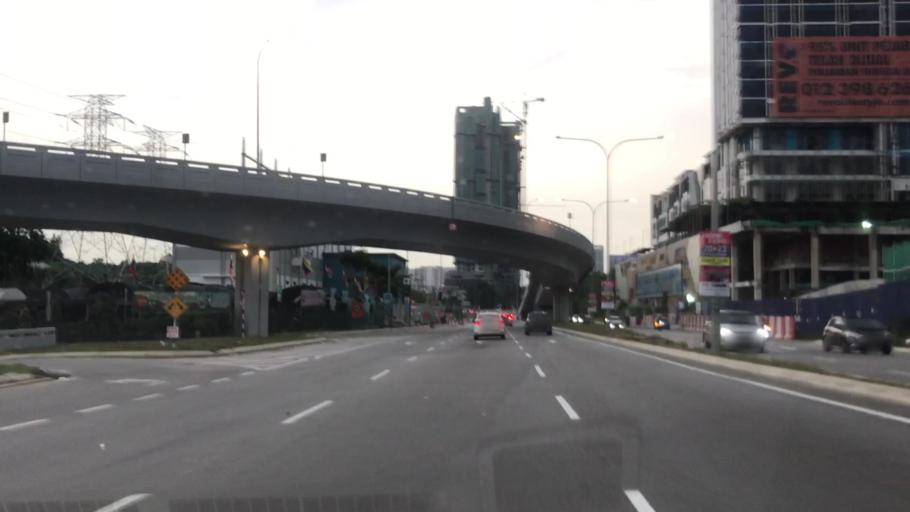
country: MY
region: Selangor
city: Kampong Baharu Balakong
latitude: 3.0513
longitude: 101.6693
